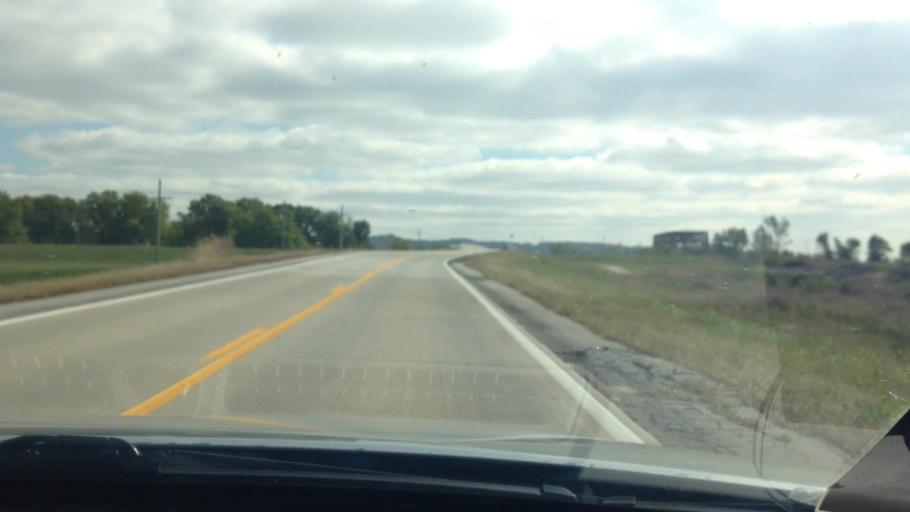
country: US
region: Kansas
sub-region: Leavenworth County
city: Lansing
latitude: 39.2760
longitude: -94.8292
